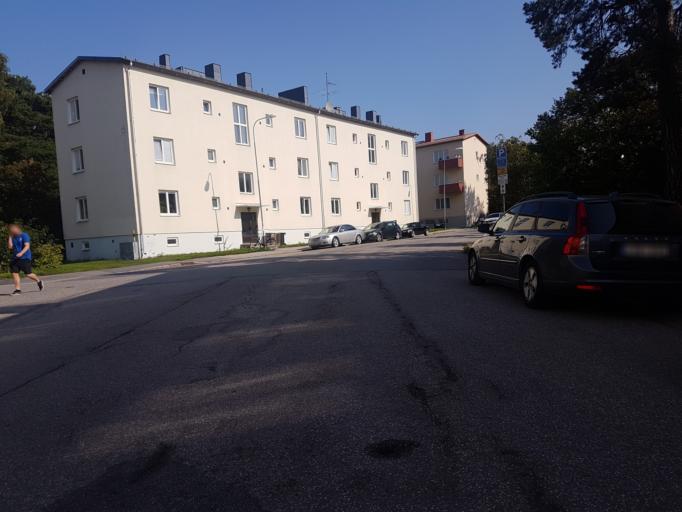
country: SE
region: Stockholm
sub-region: Stockholms Kommun
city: Arsta
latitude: 59.2974
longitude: 18.0928
